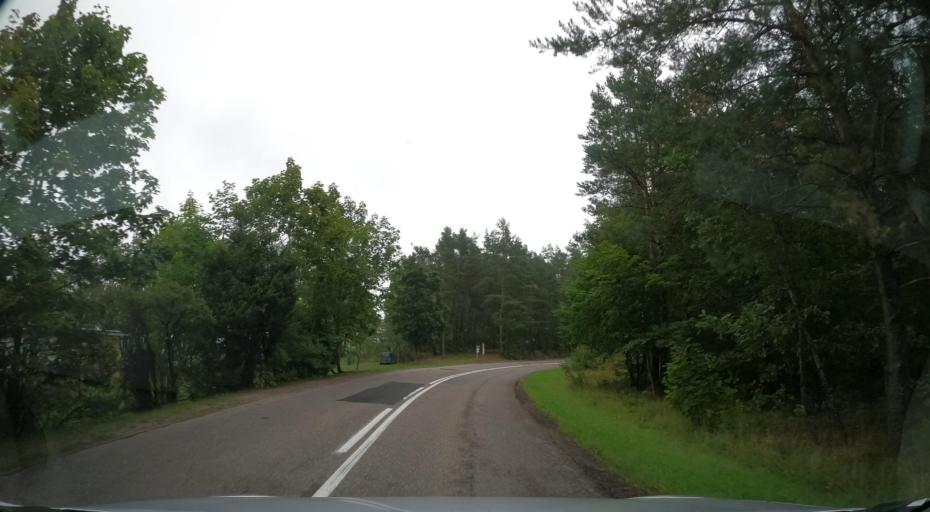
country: PL
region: Pomeranian Voivodeship
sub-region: Powiat wejherowski
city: Linia
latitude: 54.4672
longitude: 17.9887
